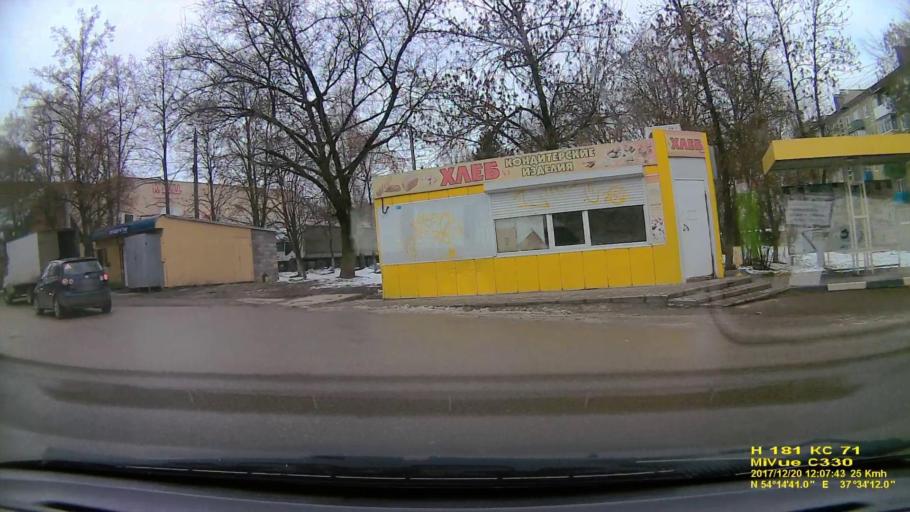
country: RU
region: Tula
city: Gorelki
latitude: 54.2448
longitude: 37.5698
